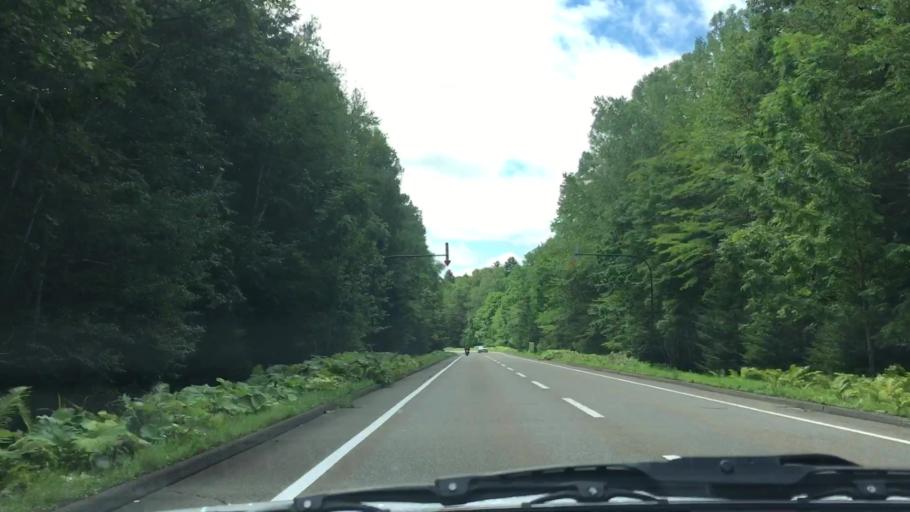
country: JP
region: Hokkaido
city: Kitami
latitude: 43.3999
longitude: 143.9279
